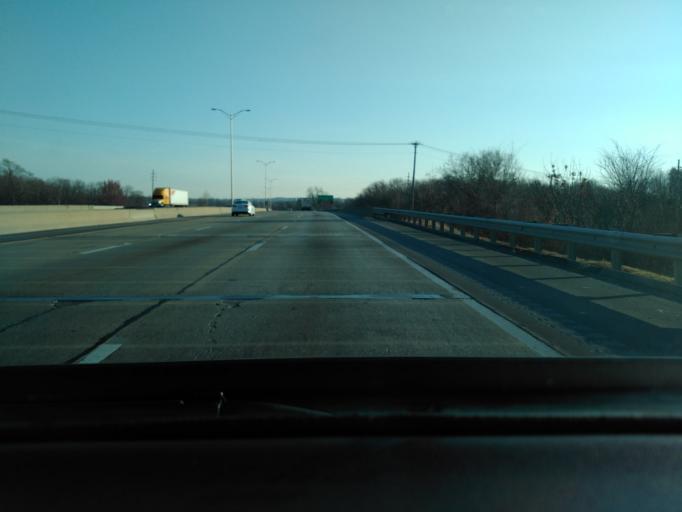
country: US
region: Illinois
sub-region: Saint Clair County
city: Centreville
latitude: 38.5568
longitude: -90.1487
